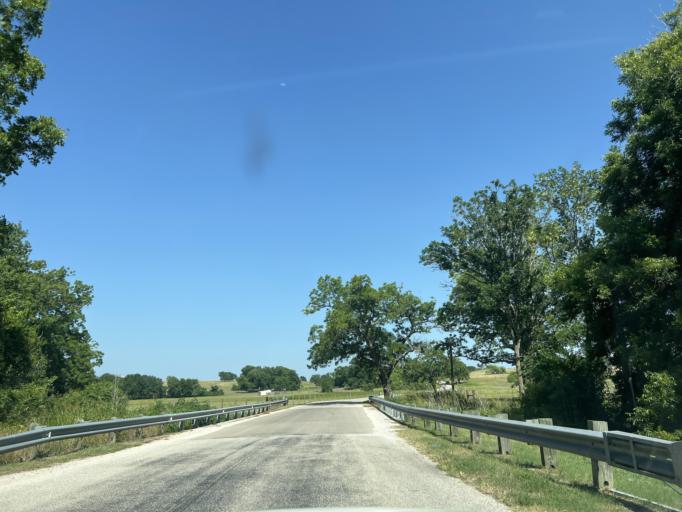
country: US
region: Texas
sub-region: Washington County
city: Brenham
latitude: 30.1728
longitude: -96.3411
